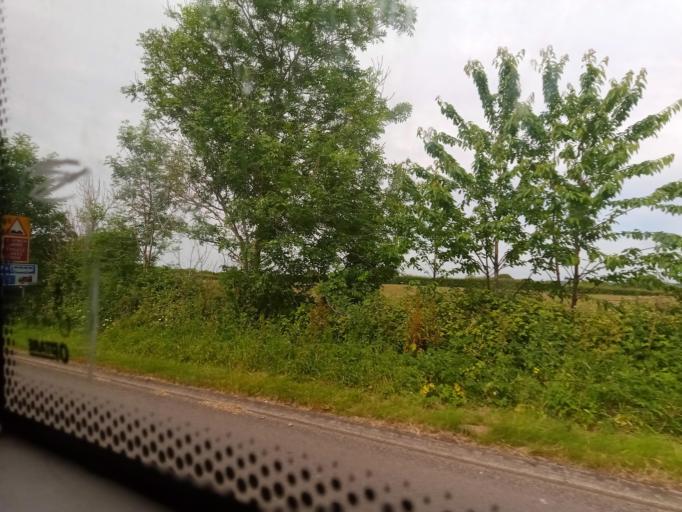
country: GB
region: Wales
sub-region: Anglesey
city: Llanfairpwllgwyngyll
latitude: 53.2272
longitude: -4.1887
